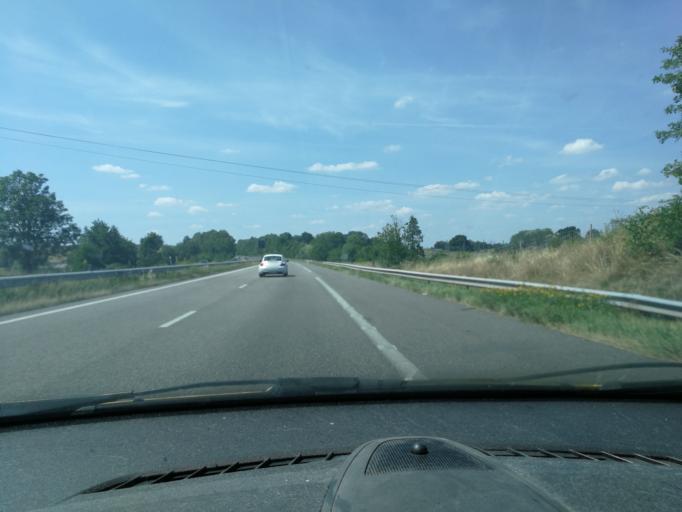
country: FR
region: Lorraine
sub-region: Departement de la Moselle
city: Phalsbourg
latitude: 48.7755
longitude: 7.2673
